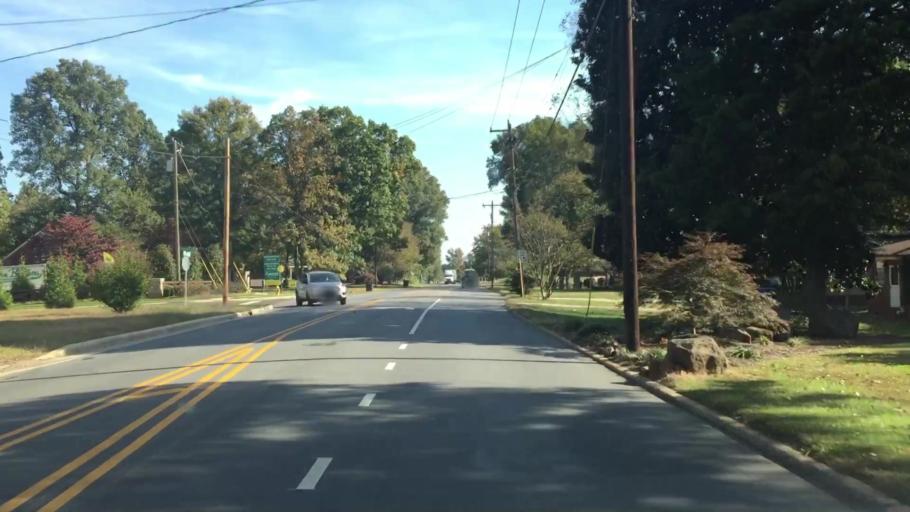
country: US
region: North Carolina
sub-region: Iredell County
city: Mooresville
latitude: 35.5803
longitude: -80.7956
